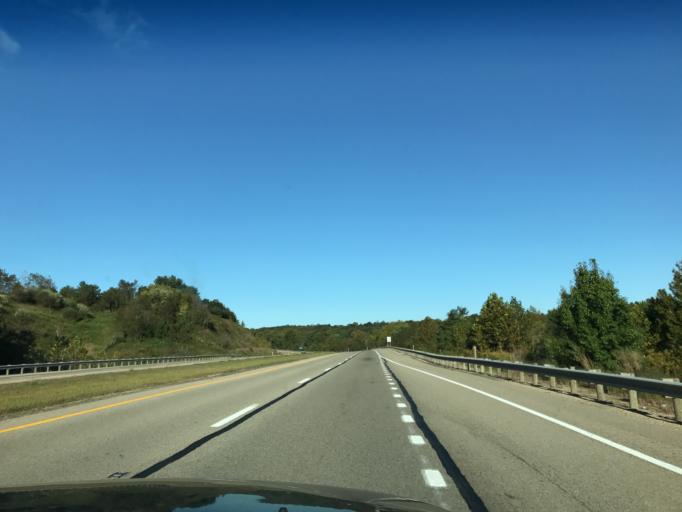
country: US
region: West Virginia
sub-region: Wood County
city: Blennerhassett
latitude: 39.2545
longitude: -81.6181
